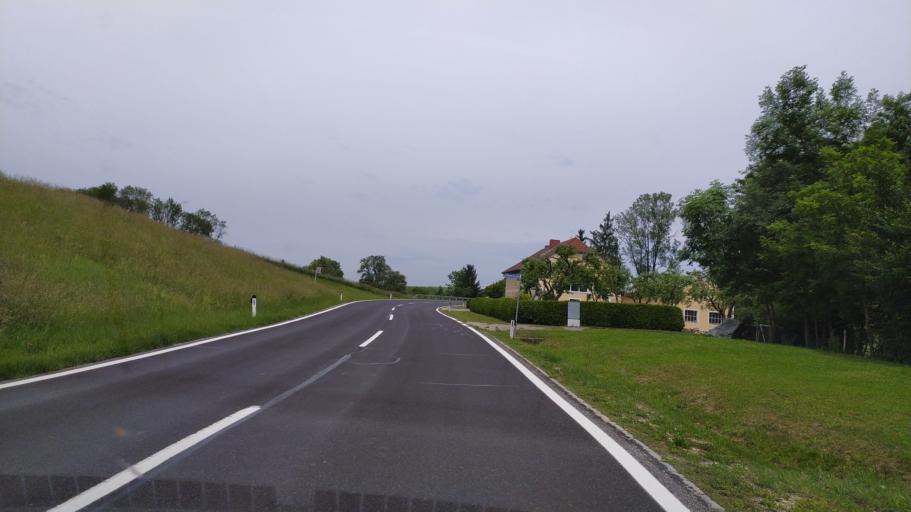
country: AT
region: Lower Austria
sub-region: Politischer Bezirk Amstetten
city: Strengberg
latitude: 48.1409
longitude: 14.6240
